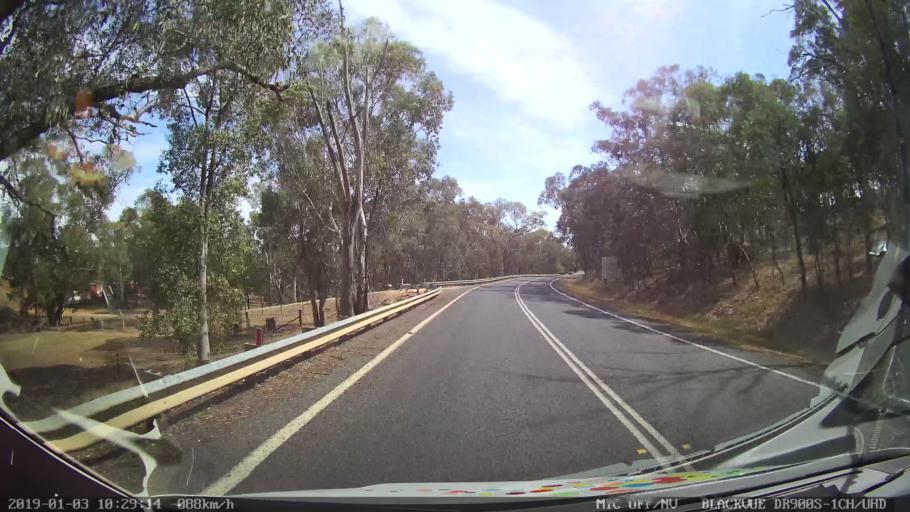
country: AU
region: New South Wales
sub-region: Young
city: Young
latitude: -34.3767
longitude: 148.2593
